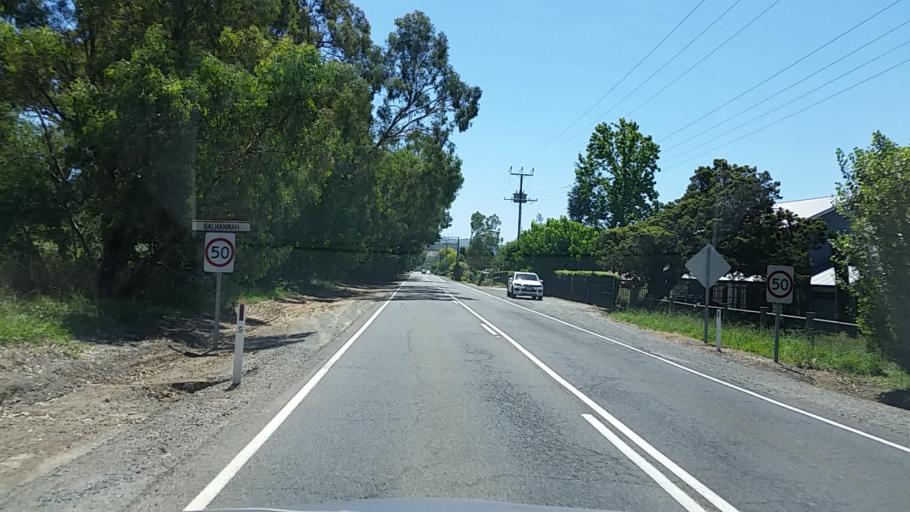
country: AU
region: South Australia
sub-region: Adelaide Hills
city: Balhannah
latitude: -34.9964
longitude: 138.8305
